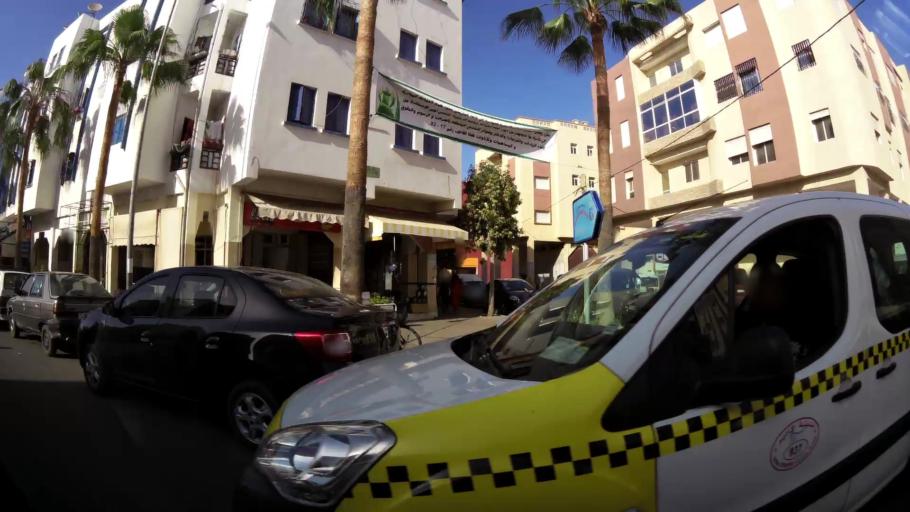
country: MA
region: Souss-Massa-Draa
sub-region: Inezgane-Ait Mellou
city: Inezgane
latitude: 30.3635
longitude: -9.5265
